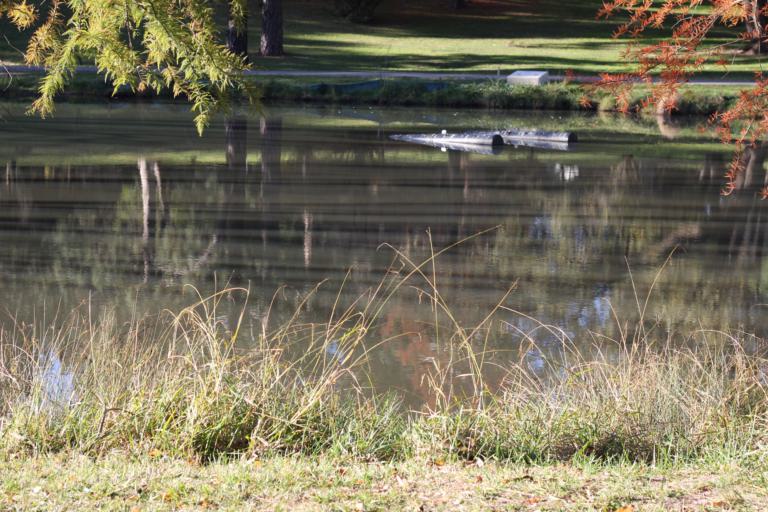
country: AU
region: Australian Capital Territory
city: Acton
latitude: -35.2985
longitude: 149.0897
